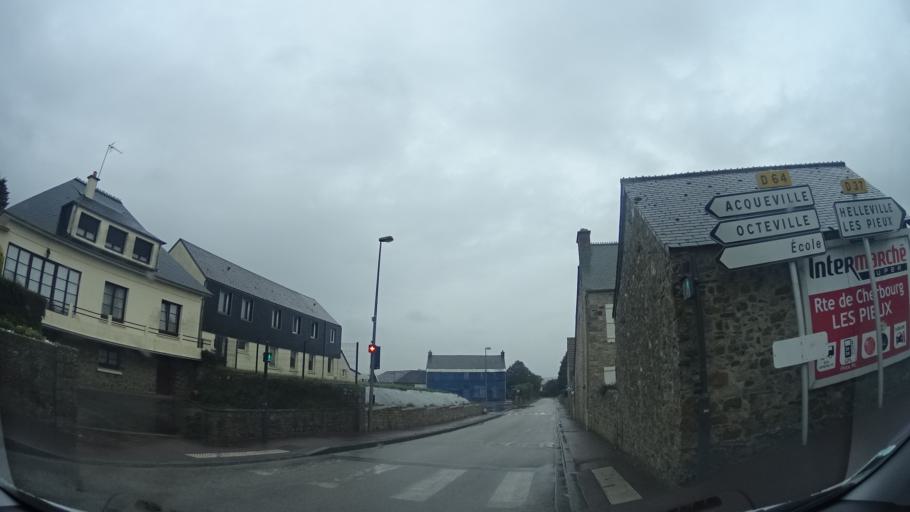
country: FR
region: Lower Normandy
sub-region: Departement de la Manche
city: Urville-Nacqueville
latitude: 49.5945
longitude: -1.7728
